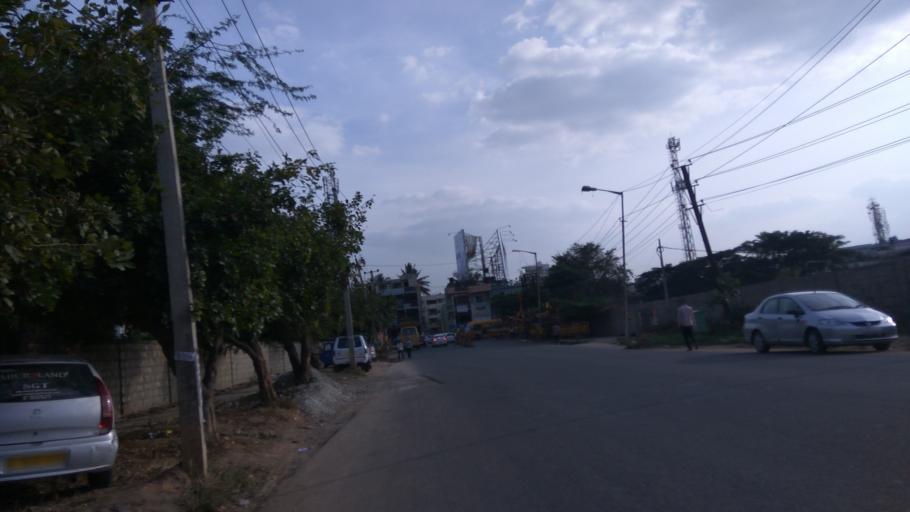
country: IN
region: Karnataka
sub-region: Bangalore Urban
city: Bangalore
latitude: 12.9568
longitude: 77.6916
